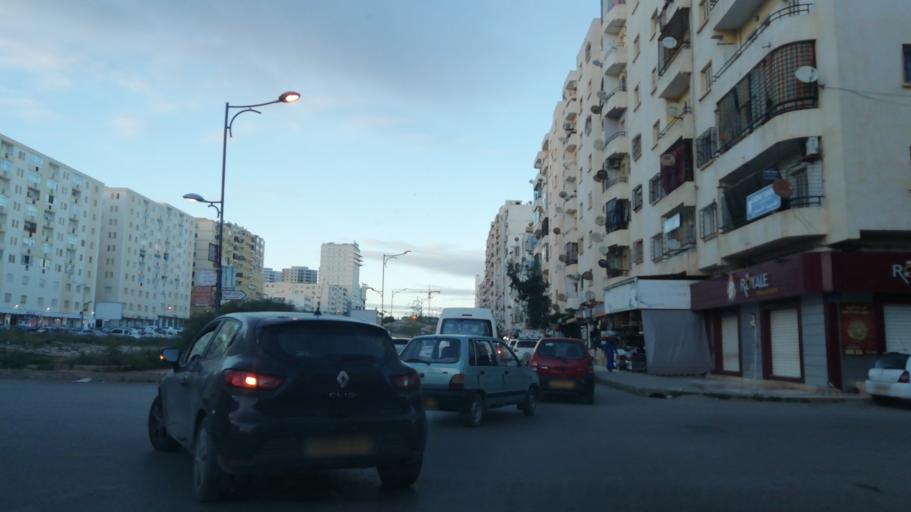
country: DZ
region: Oran
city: Bir el Djir
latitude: 35.7023
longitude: -0.5607
